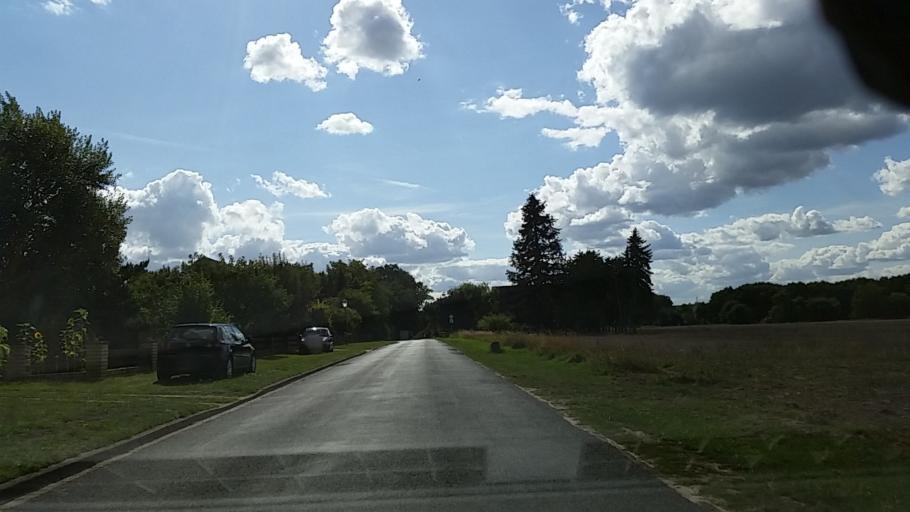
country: DE
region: Lower Saxony
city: Barnstedt
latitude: 53.1264
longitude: 10.4253
